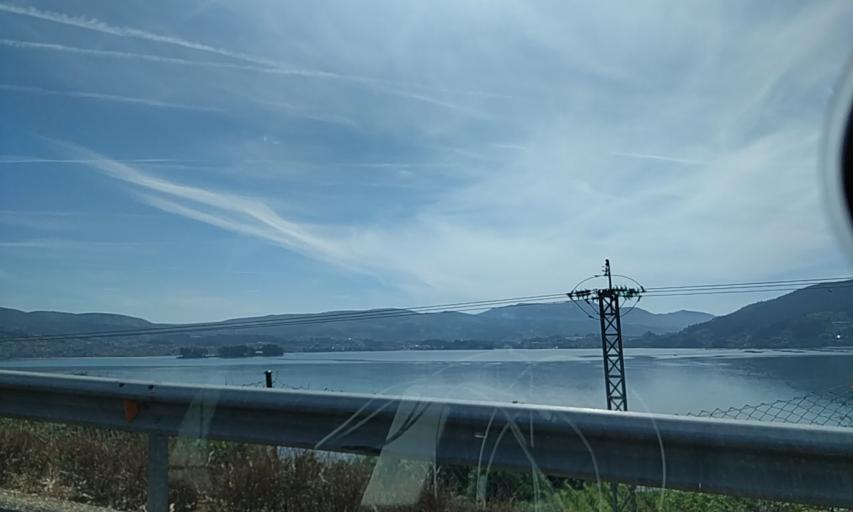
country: ES
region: Galicia
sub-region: Provincia de Pontevedra
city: Redondela
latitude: 42.3175
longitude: -8.6599
